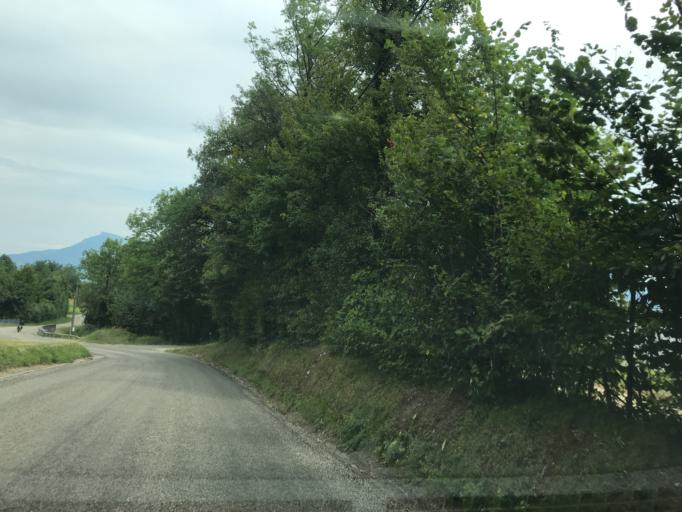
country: FR
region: Rhone-Alpes
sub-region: Departement de l'Isere
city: Chapareillan
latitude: 45.4646
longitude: 5.9666
